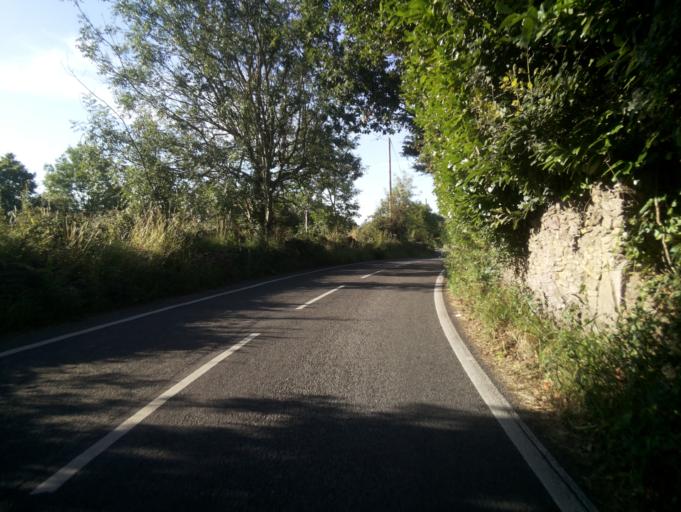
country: GB
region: England
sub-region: South Gloucestershire
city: Kingswood
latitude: 51.4350
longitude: -2.5120
